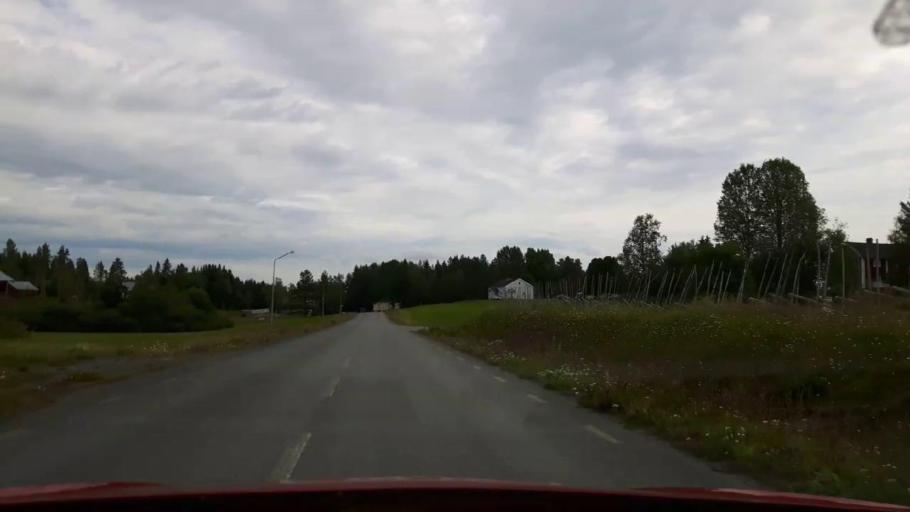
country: SE
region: Jaemtland
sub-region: OEstersunds Kommun
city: Lit
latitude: 63.4151
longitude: 15.2475
